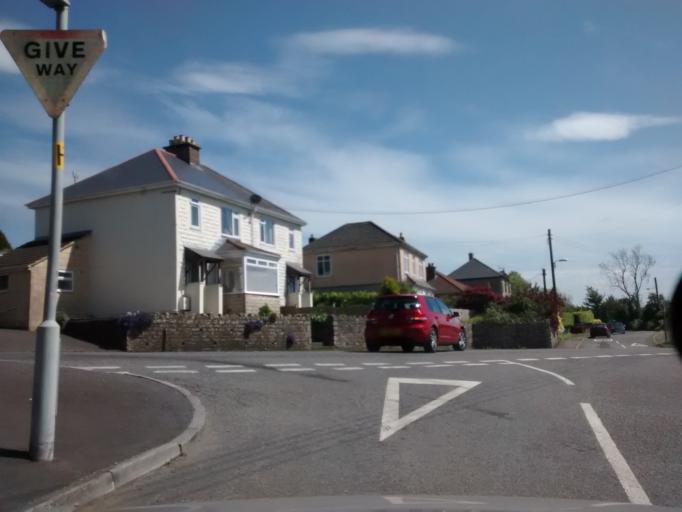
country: GB
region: England
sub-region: Bath and North East Somerset
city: Radstock
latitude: 51.3000
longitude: -2.4539
